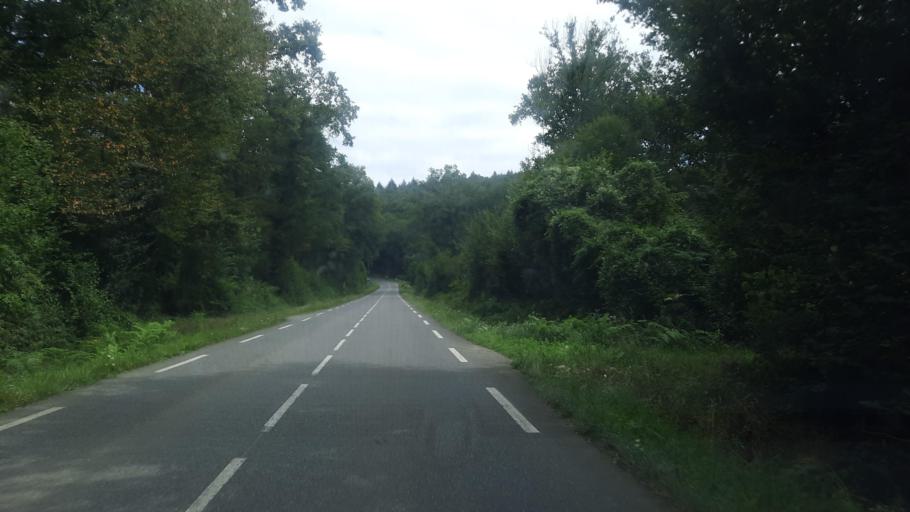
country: FR
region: Midi-Pyrenees
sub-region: Departement des Hautes-Pyrenees
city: Trie-sur-Baise
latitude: 43.2987
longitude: 0.4291
